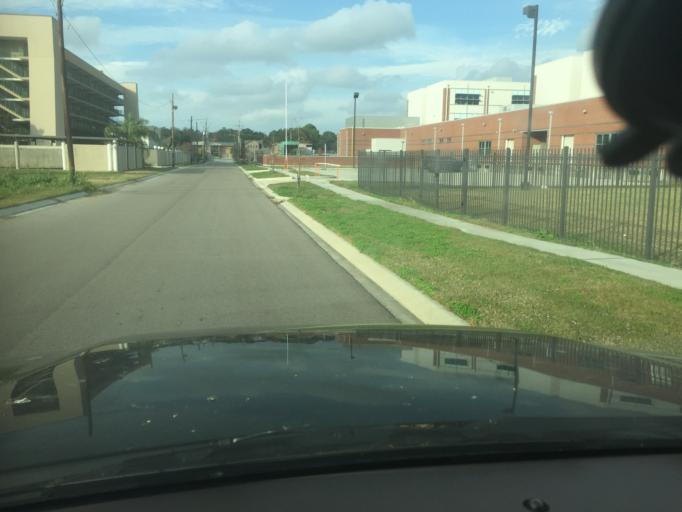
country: US
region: Louisiana
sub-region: Orleans Parish
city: New Orleans
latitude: 29.9970
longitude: -90.0841
